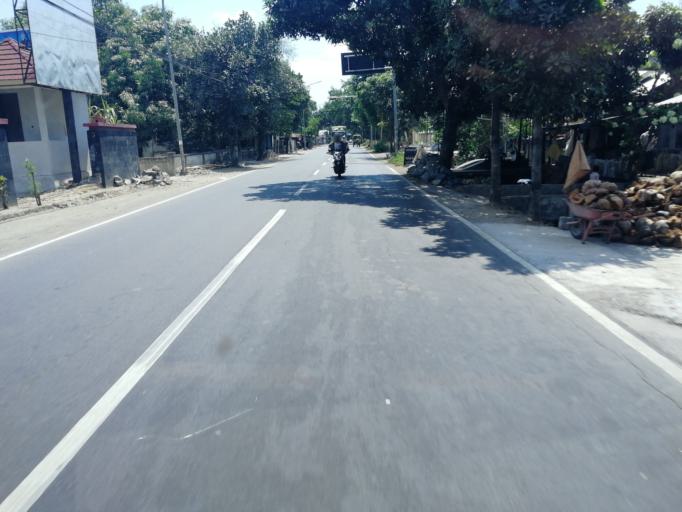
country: ID
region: West Nusa Tenggara
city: Jelateng Timur
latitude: -8.7026
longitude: 116.0949
